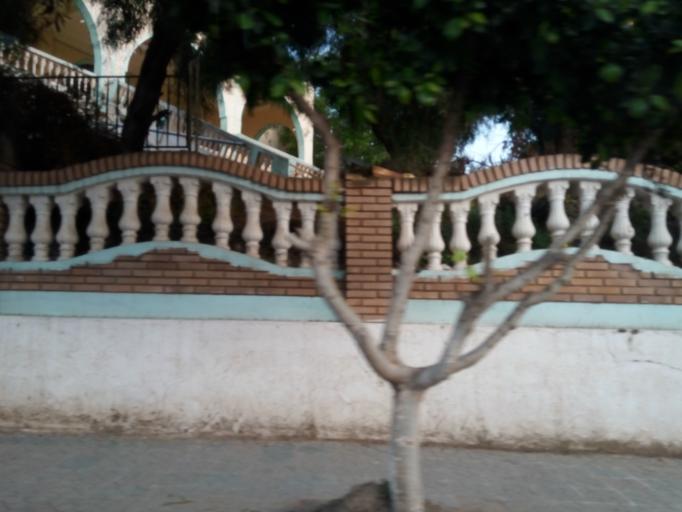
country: DZ
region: Tipaza
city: Bou Ismail
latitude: 36.6247
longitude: 2.6571
